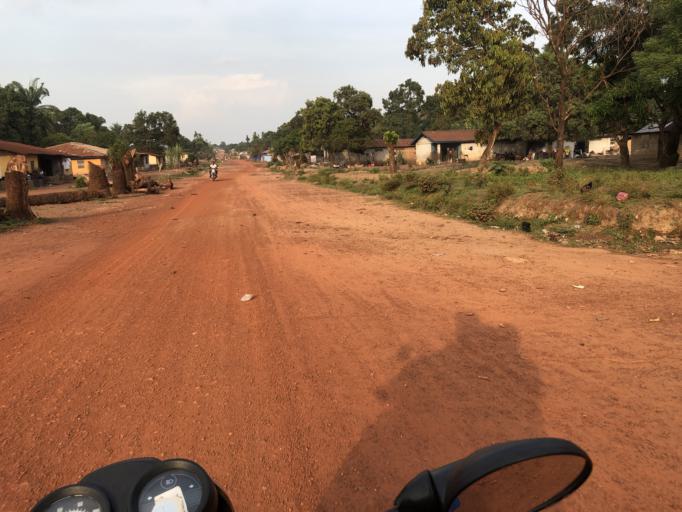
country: SL
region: Northern Province
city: Yonibana
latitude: 8.4673
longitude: -12.2087
